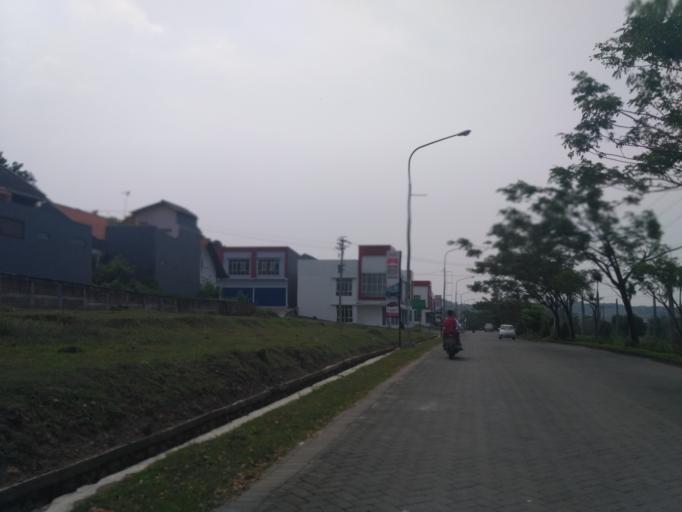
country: ID
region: Central Java
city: Mranggen
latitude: -7.0665
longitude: 110.4610
